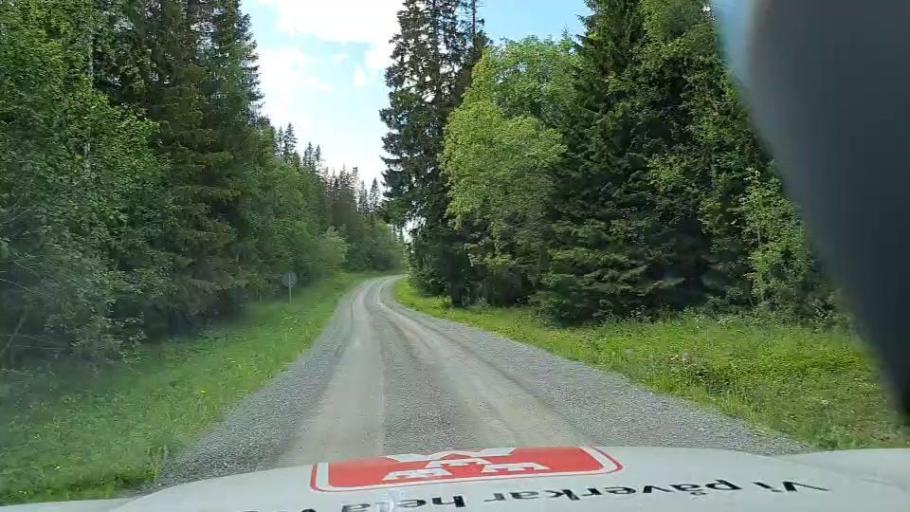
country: SE
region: Jaemtland
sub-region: Krokoms Kommun
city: Valla
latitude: 63.5666
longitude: 13.7938
